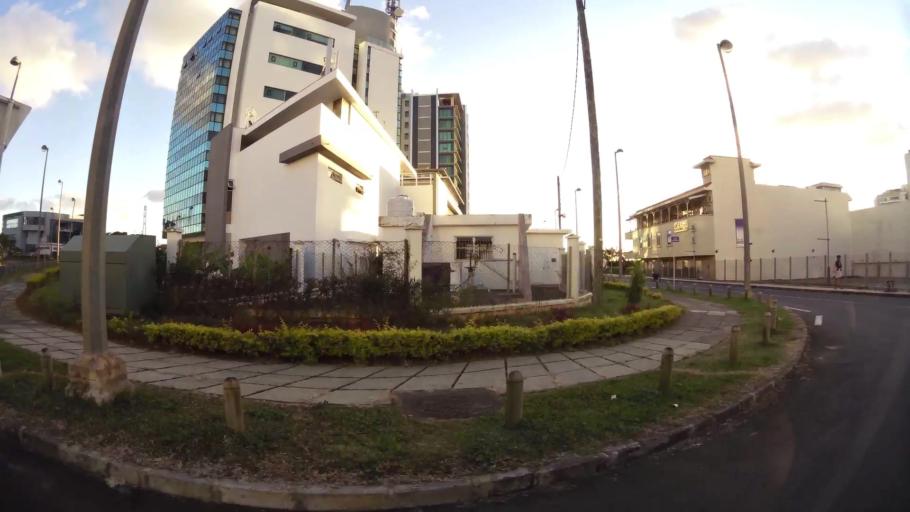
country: MU
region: Plaines Wilhems
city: Ebene
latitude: -20.2444
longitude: 57.4888
